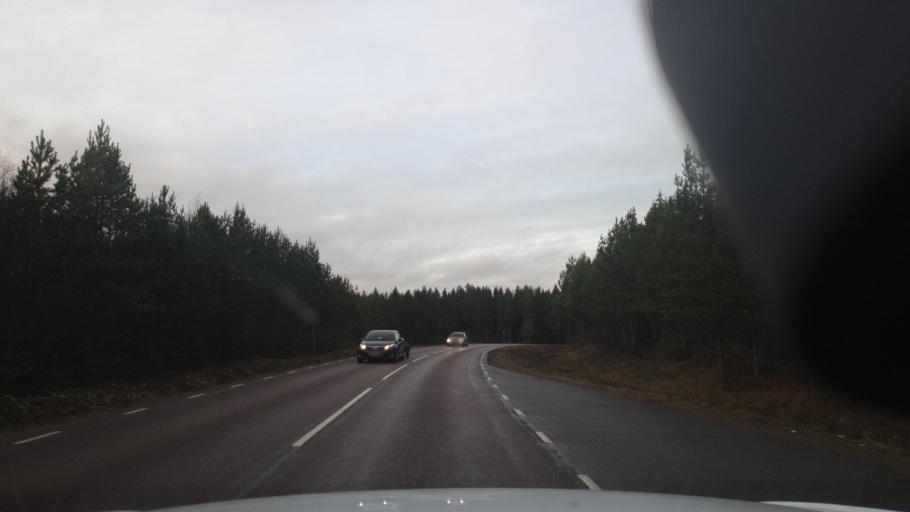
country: SE
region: Vaermland
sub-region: Eda Kommun
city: Amotfors
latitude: 59.7312
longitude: 12.1721
